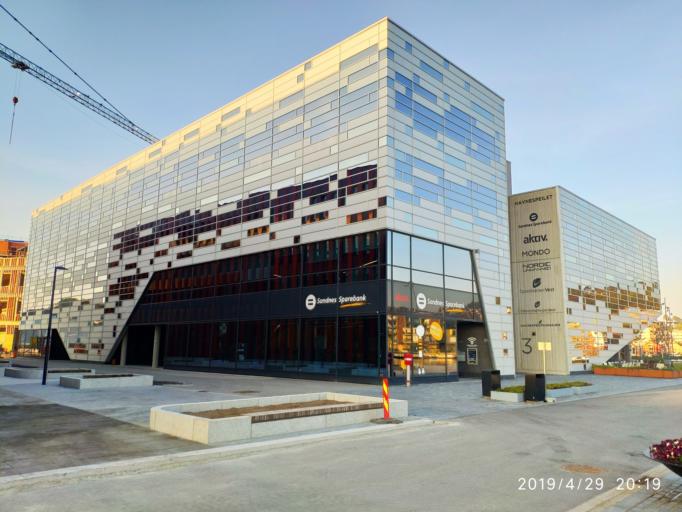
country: NO
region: Rogaland
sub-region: Sandnes
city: Sandnes
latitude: 58.8529
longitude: 5.7420
